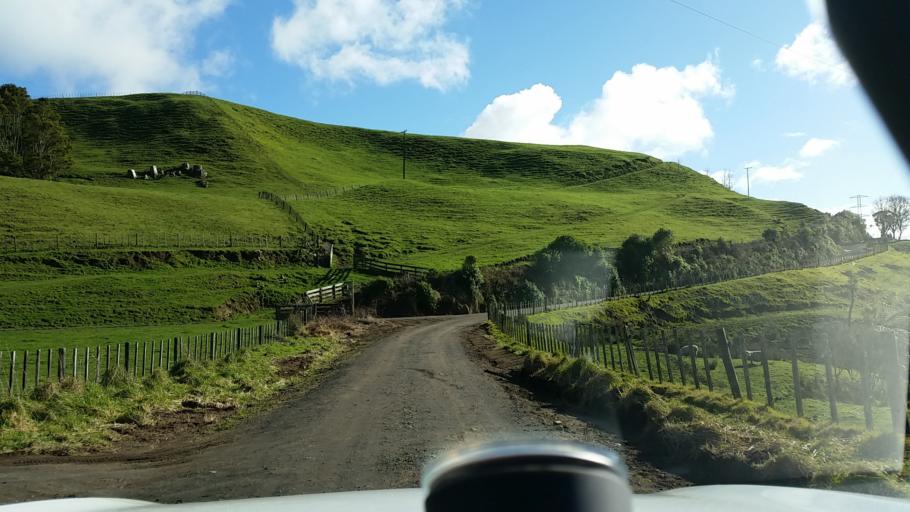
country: NZ
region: Taranaki
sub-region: South Taranaki District
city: Eltham
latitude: -39.4577
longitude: 174.3696
